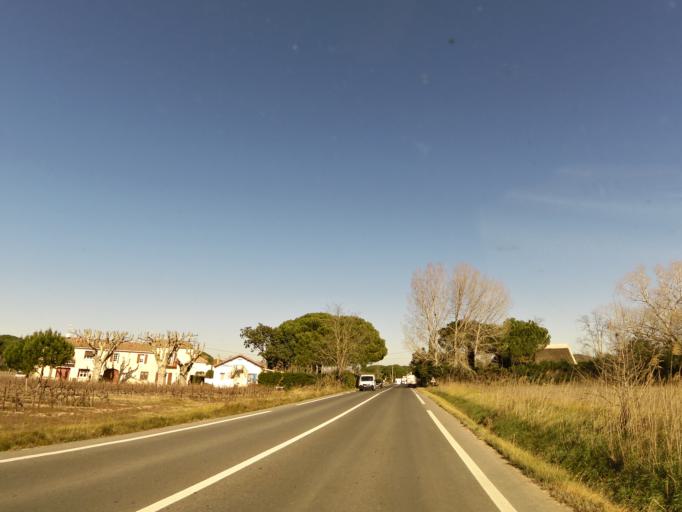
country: FR
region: Languedoc-Roussillon
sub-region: Departement du Gard
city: Aigues-Mortes
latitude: 43.5805
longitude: 4.2049
